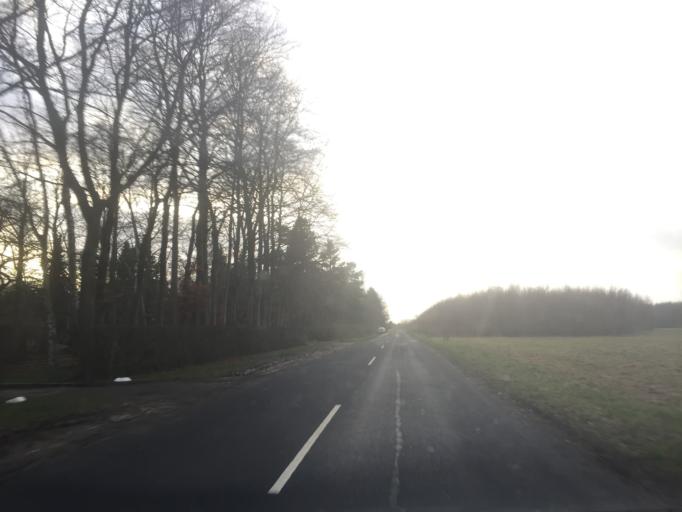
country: DK
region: Capital Region
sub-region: Albertslund Kommune
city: Albertslund
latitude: 55.6902
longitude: 12.3406
